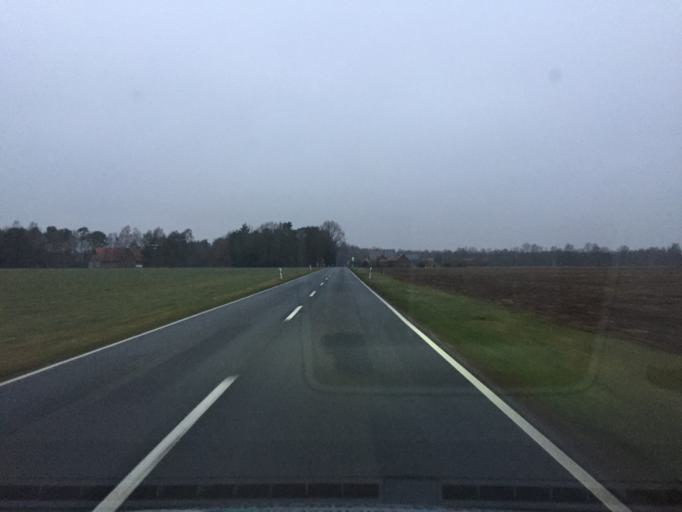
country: DE
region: Lower Saxony
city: Kirchdorf
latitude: 52.6150
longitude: 8.8937
